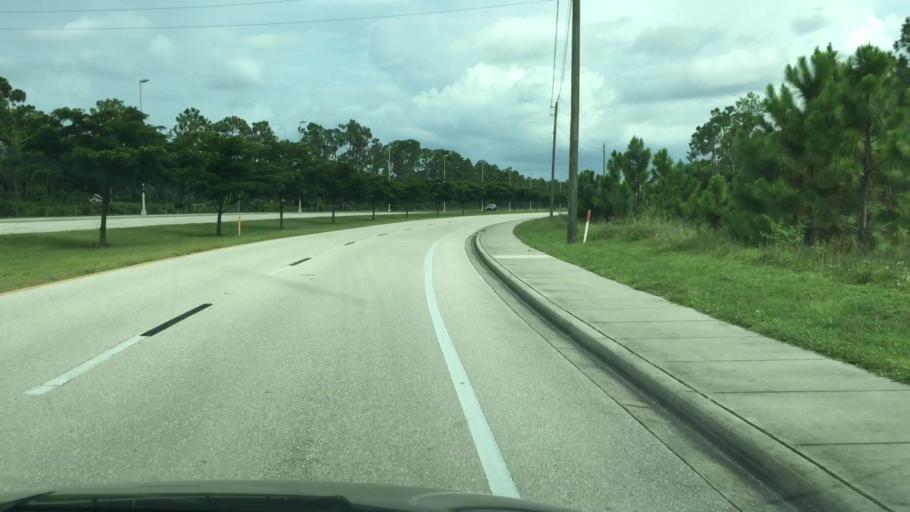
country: US
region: Florida
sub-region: Lee County
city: Three Oaks
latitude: 26.4653
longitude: -81.7900
